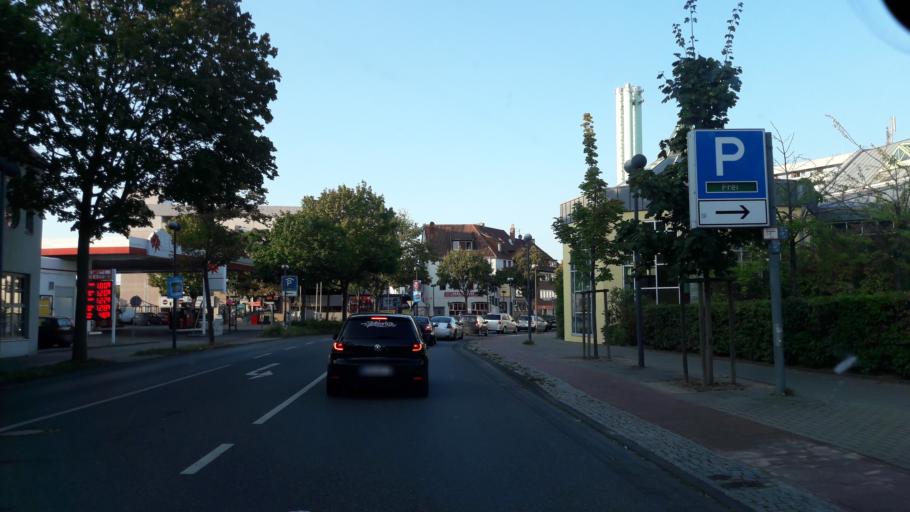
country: DE
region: Lower Saxony
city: Hildesheim
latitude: 52.1572
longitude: 9.9496
